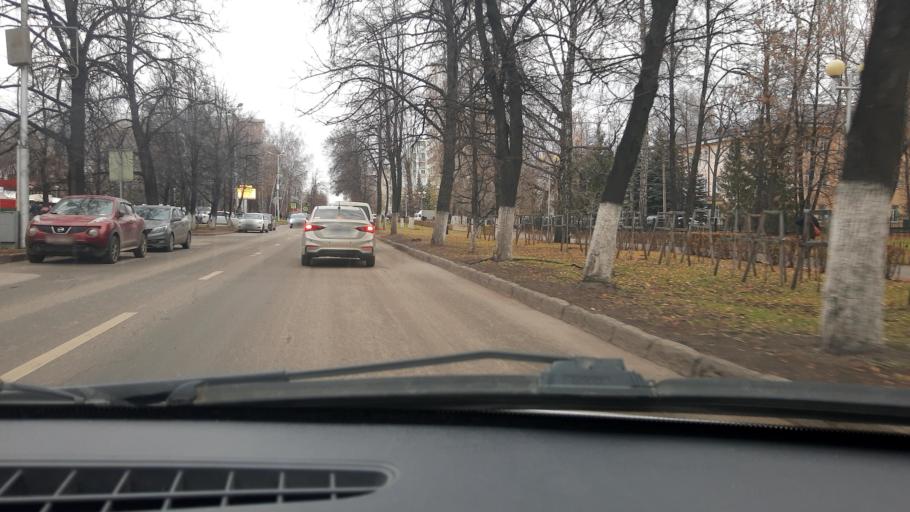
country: RU
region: Bashkortostan
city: Avdon
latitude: 54.7010
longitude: 55.8307
